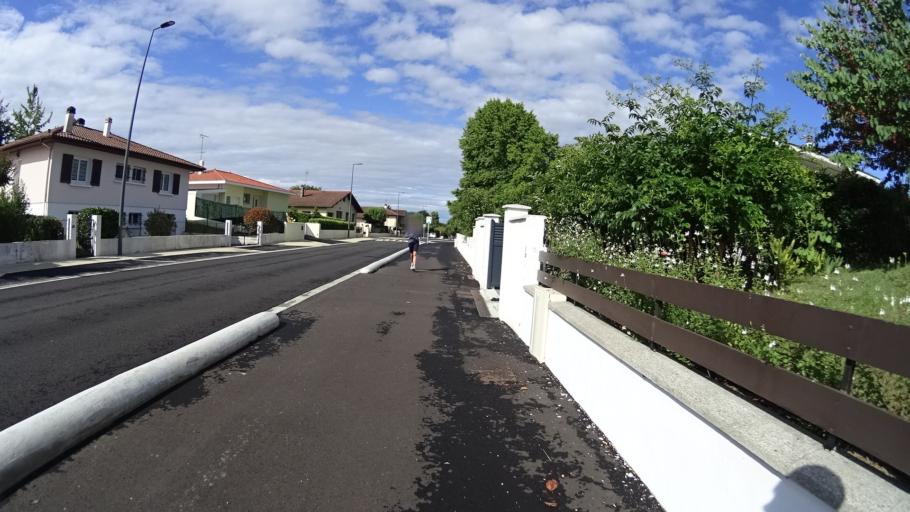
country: FR
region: Aquitaine
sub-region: Departement des Landes
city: Dax
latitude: 43.6995
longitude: -1.0700
